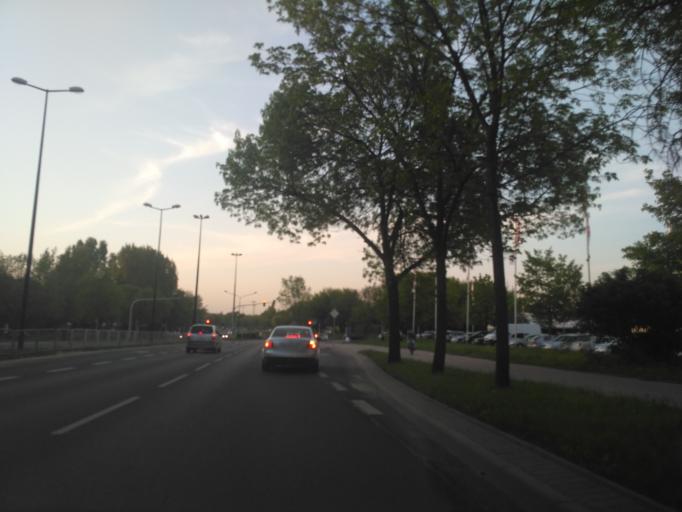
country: PL
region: Lublin Voivodeship
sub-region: Powiat lubelski
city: Lublin
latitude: 51.2665
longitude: 22.5584
